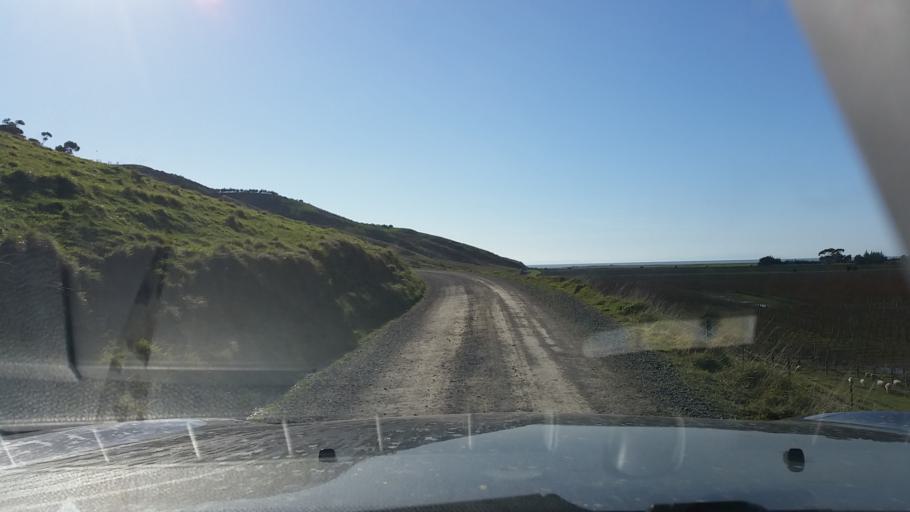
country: NZ
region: Marlborough
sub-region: Marlborough District
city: Blenheim
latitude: -41.6680
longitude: 174.1408
